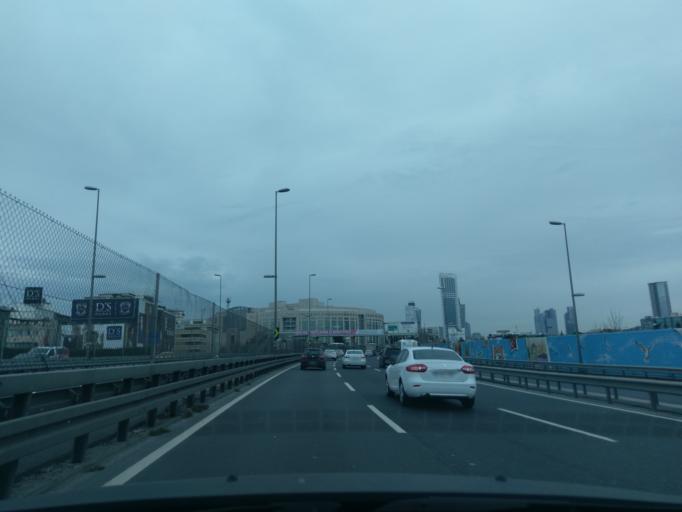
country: TR
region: Istanbul
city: Sisli
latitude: 41.0669
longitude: 28.9733
